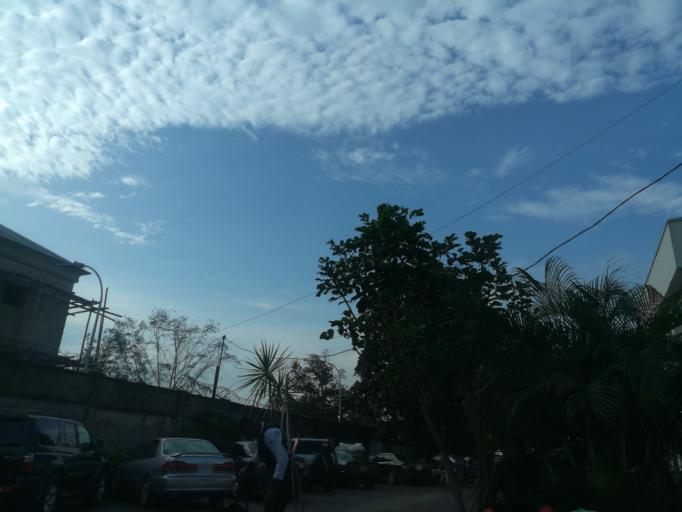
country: NG
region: Lagos
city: Ikeja
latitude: 6.5954
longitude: 3.3481
